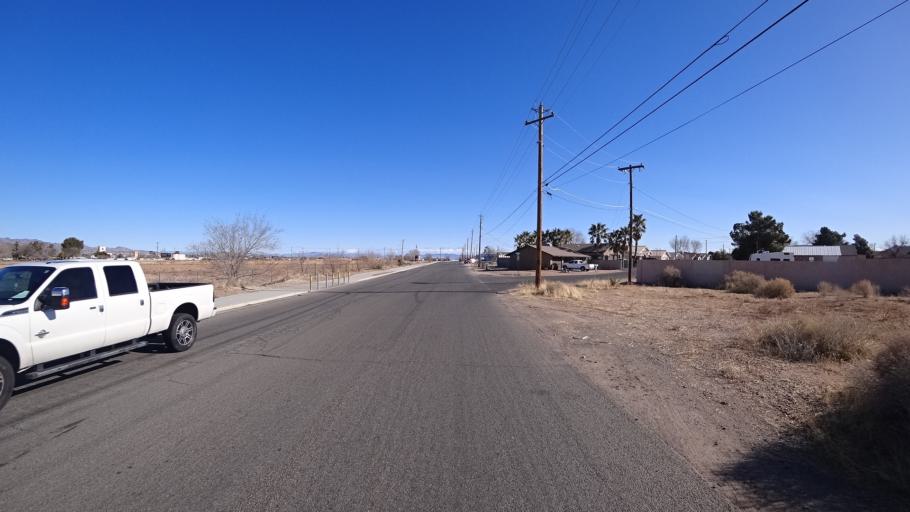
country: US
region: Arizona
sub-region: Mohave County
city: Kingman
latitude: 35.1985
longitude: -114.0239
